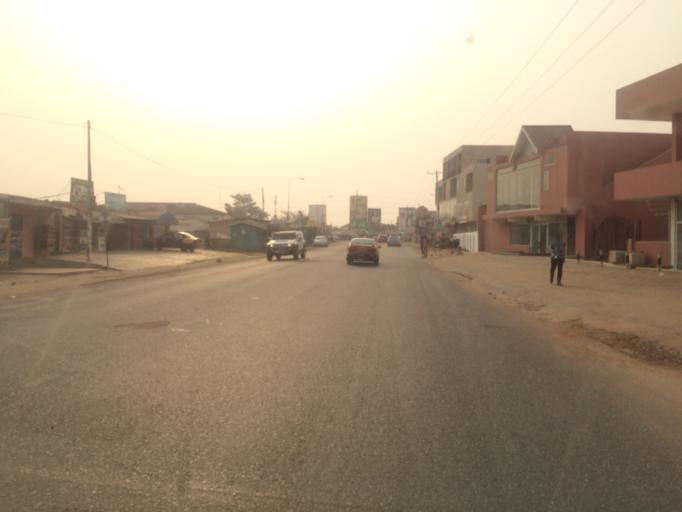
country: GH
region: Greater Accra
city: Nungua
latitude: 5.6224
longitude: -0.0719
